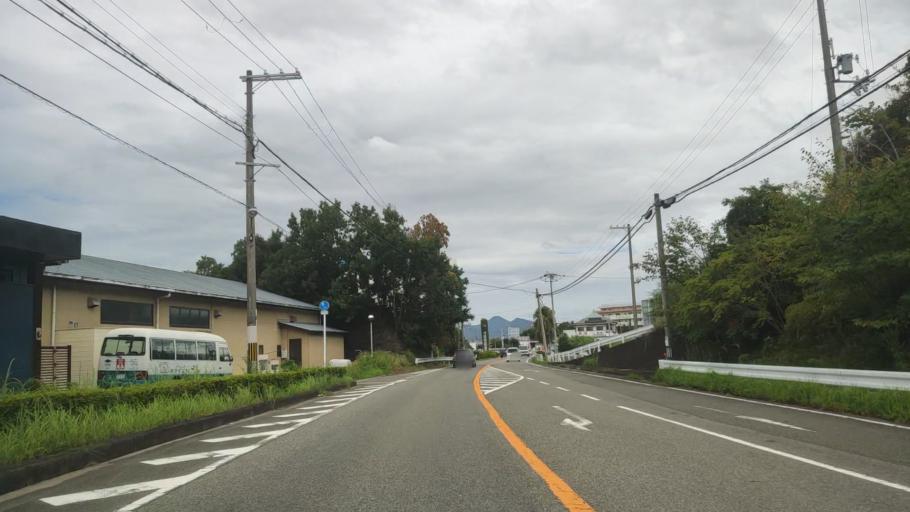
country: JP
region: Wakayama
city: Tanabe
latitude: 33.6970
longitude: 135.3881
